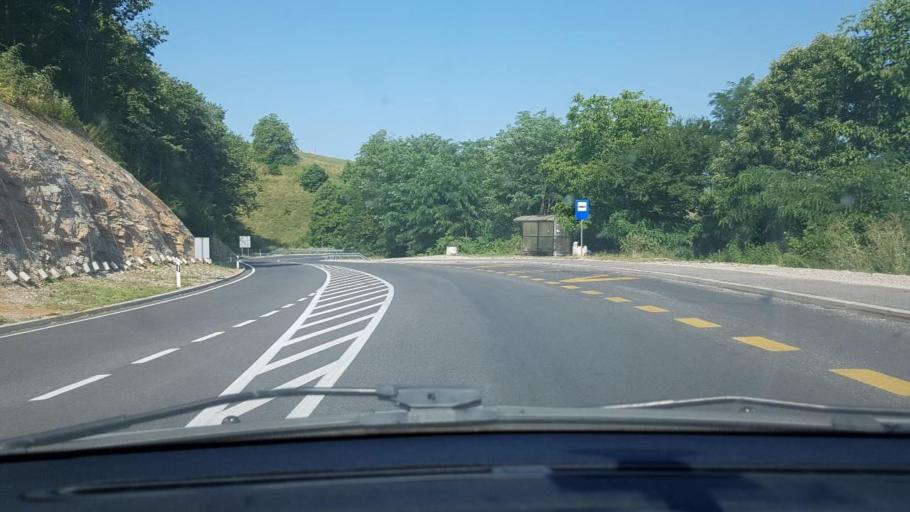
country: BA
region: Federation of Bosnia and Herzegovina
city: Skokovi
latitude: 45.0429
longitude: 15.9149
